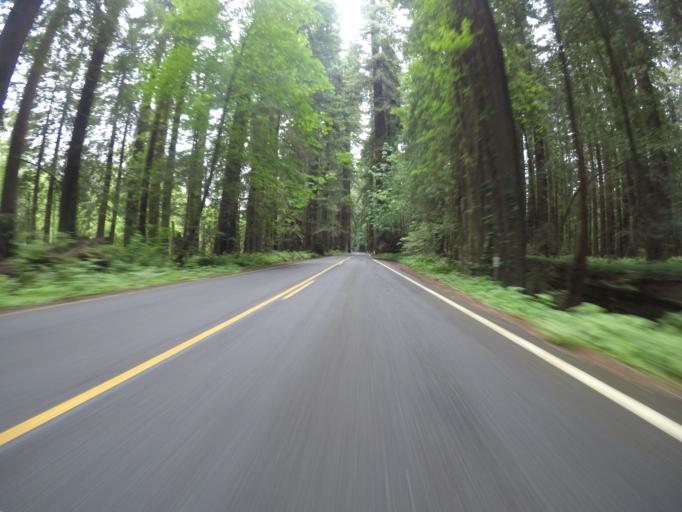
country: US
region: California
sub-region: Humboldt County
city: Rio Dell
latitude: 40.4433
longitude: -124.0226
